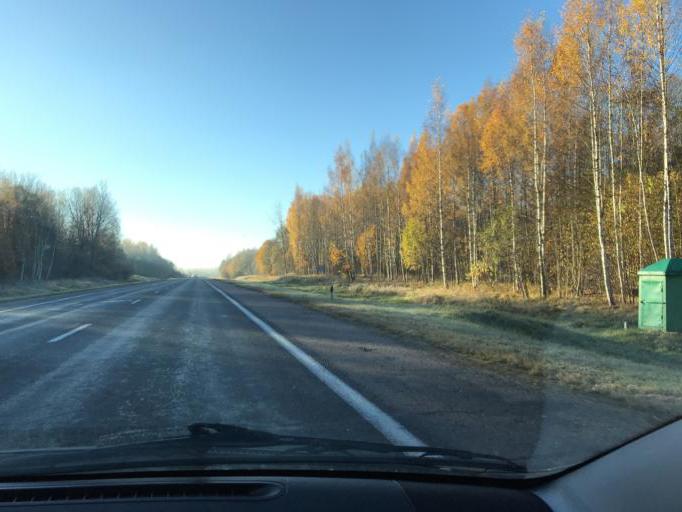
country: BY
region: Vitebsk
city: Vitebsk
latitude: 54.9312
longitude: 30.3708
